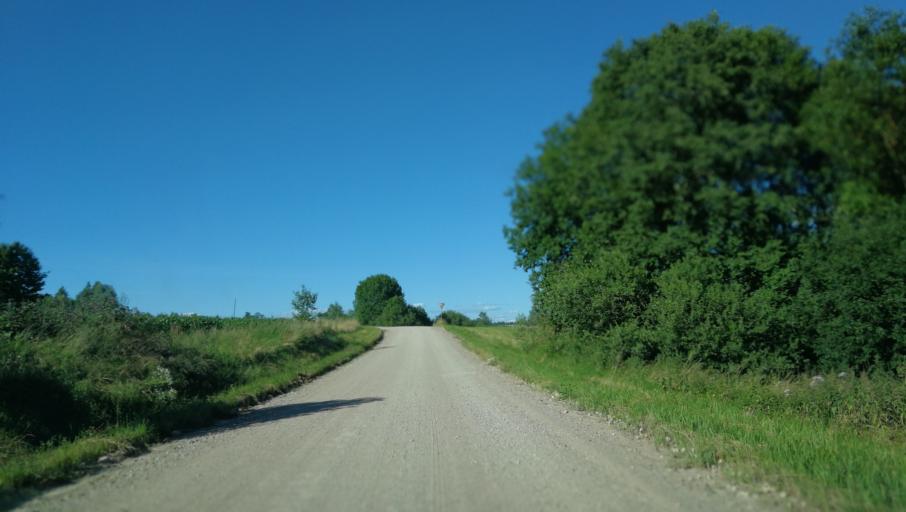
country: LV
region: Jaunpiebalga
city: Jaunpiebalga
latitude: 57.0161
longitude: 26.0520
